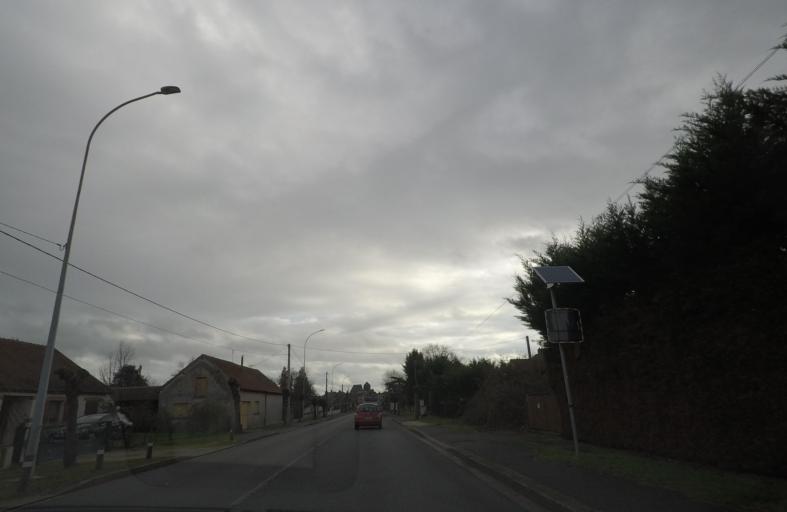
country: FR
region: Centre
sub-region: Departement du Loir-et-Cher
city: Mur-de-Sologne
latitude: 47.4137
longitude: 1.6038
